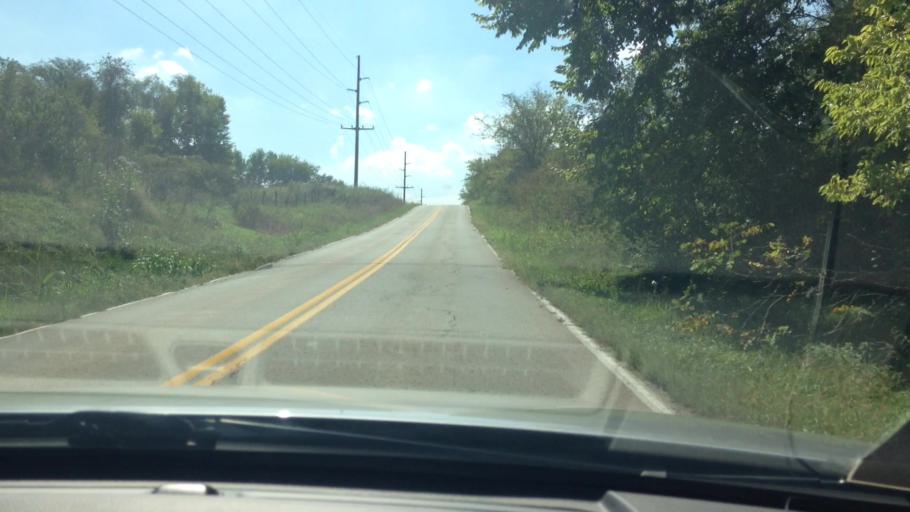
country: US
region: Missouri
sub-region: Platte County
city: Platte City
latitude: 39.3528
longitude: -94.7330
